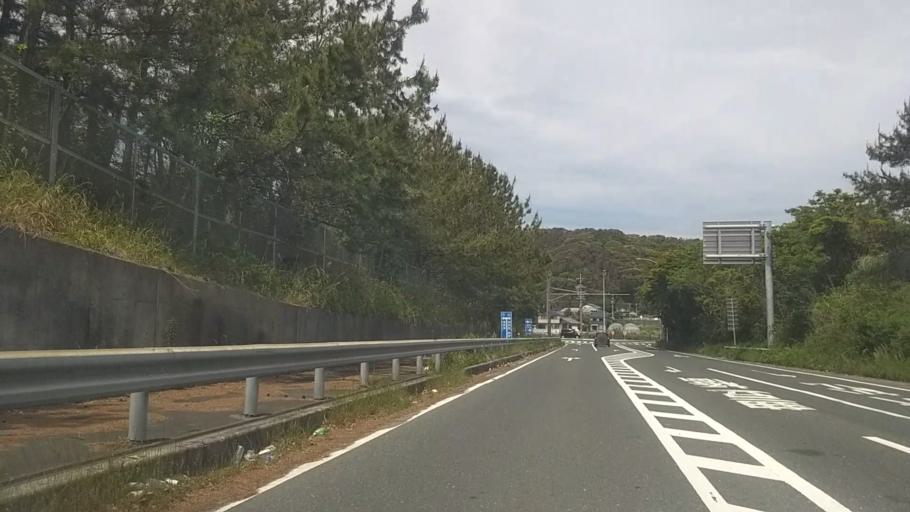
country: JP
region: Shizuoka
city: Kosai-shi
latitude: 34.6797
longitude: 137.5331
